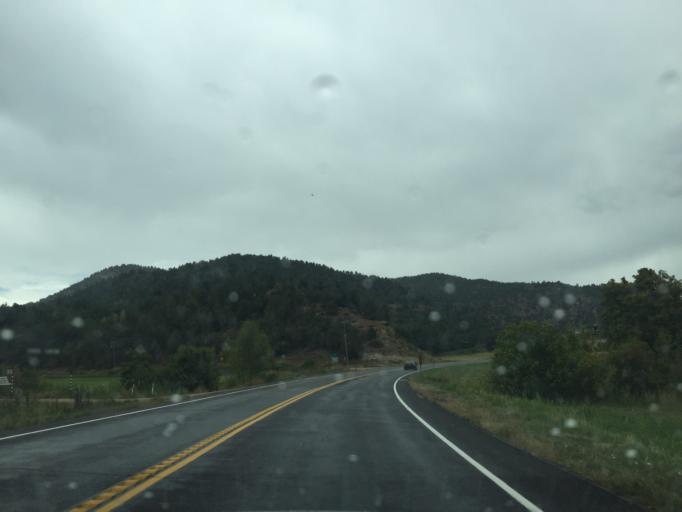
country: US
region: Utah
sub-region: Kane County
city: Kanab
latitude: 37.3394
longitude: -112.6051
